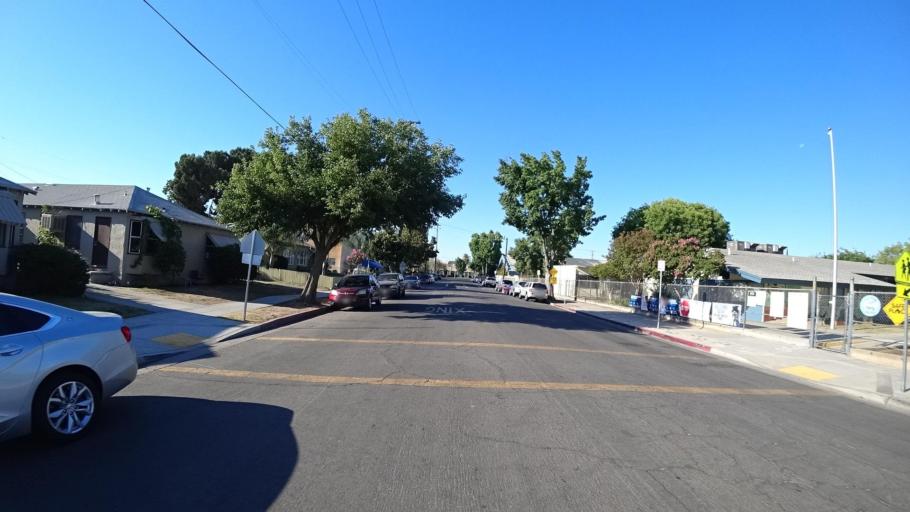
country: US
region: California
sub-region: Fresno County
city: Fresno
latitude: 36.7452
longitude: -119.7958
